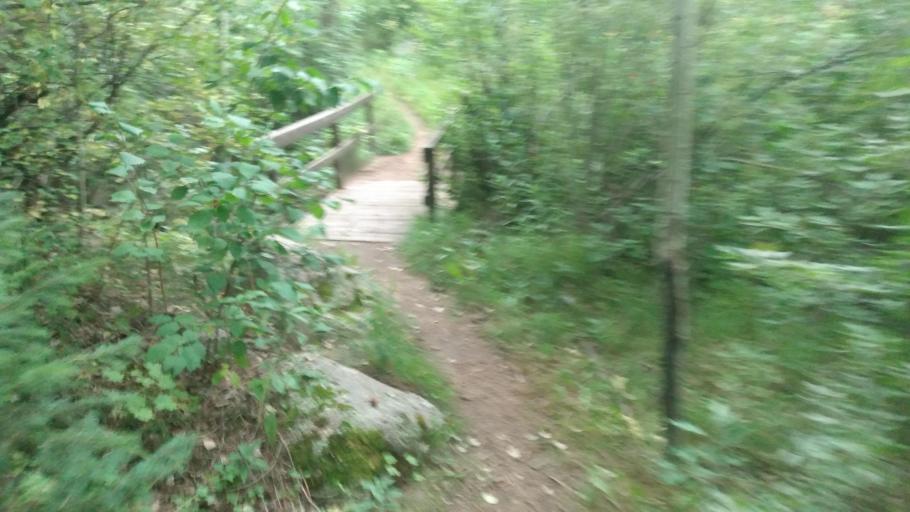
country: US
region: Colorado
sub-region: Boulder County
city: Boulder
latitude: 39.9937
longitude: -105.3083
